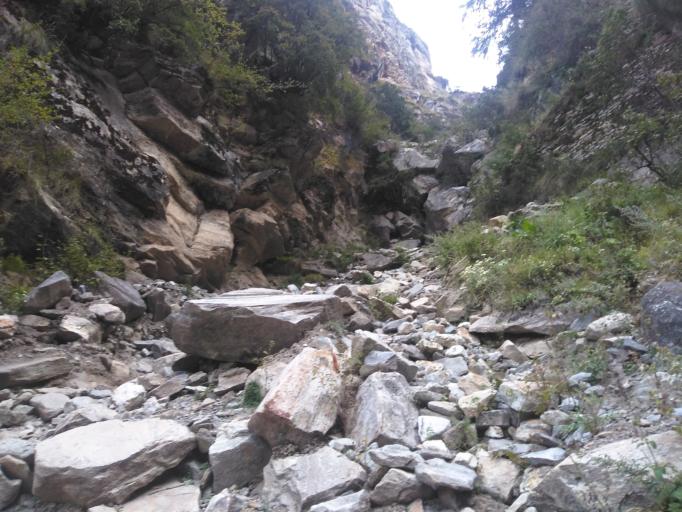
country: NP
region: Western Region
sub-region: Dhawalagiri Zone
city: Jomsom
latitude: 28.9324
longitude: 83.0465
